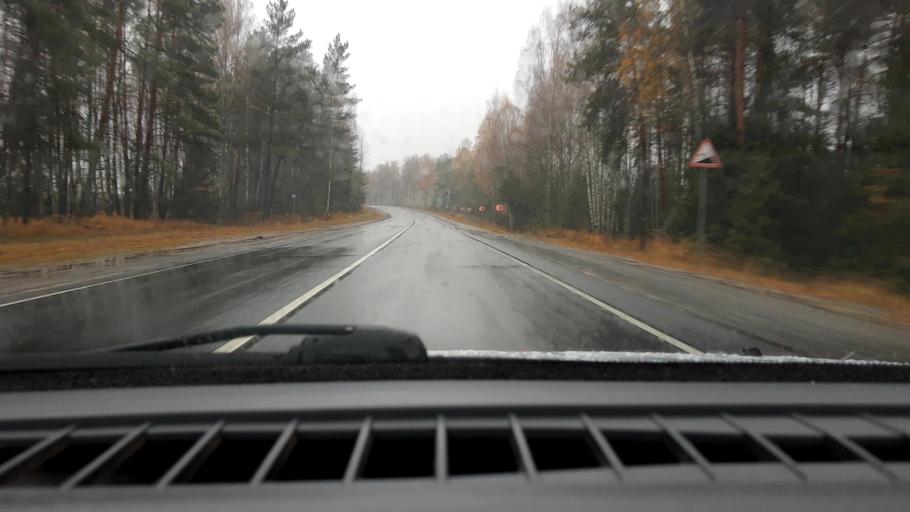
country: RU
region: Nizjnij Novgorod
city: Linda
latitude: 56.6774
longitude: 44.1469
